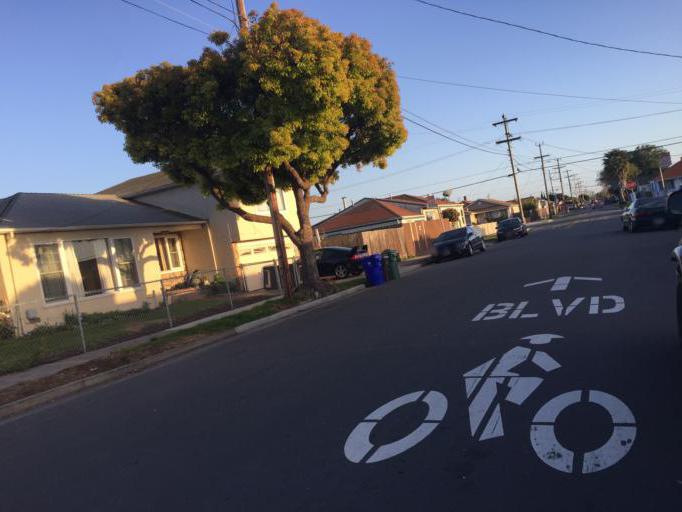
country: US
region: California
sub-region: Contra Costa County
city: San Pablo
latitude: 37.9503
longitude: -122.3521
